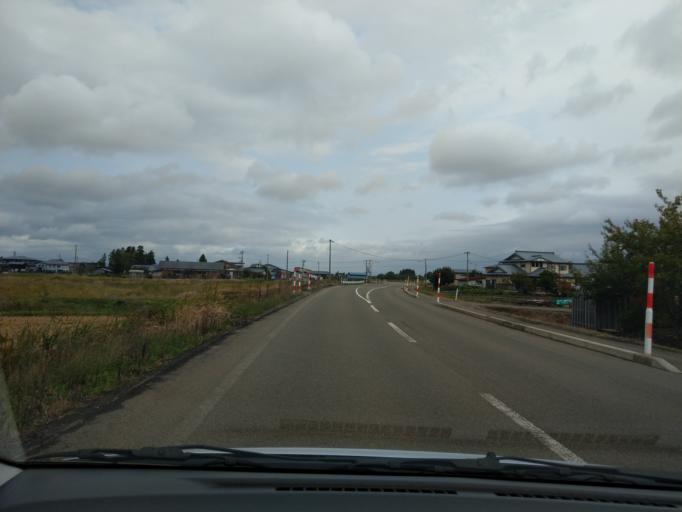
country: JP
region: Akita
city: Omagari
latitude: 39.3800
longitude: 140.4857
